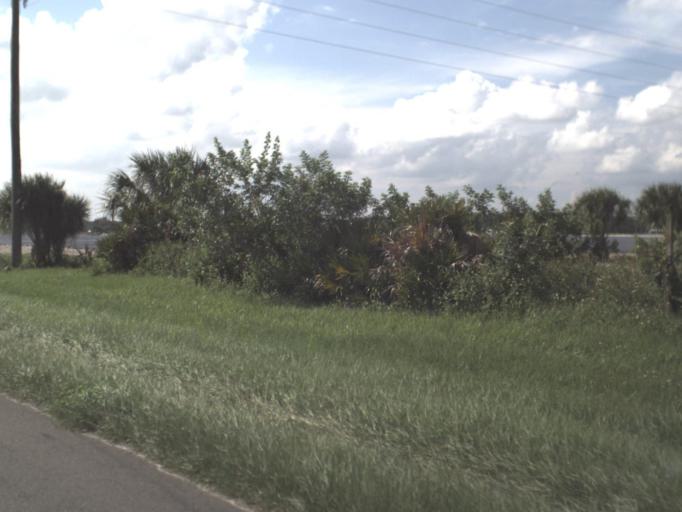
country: US
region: Florida
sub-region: Sarasota County
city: The Meadows
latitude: 27.4755
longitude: -82.3678
